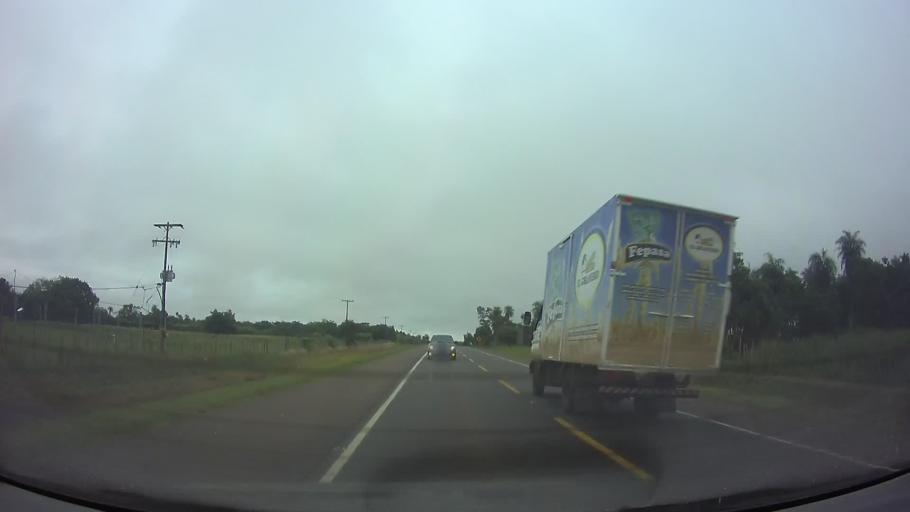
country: PY
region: Paraguari
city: Paraguari
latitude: -25.6147
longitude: -57.1799
